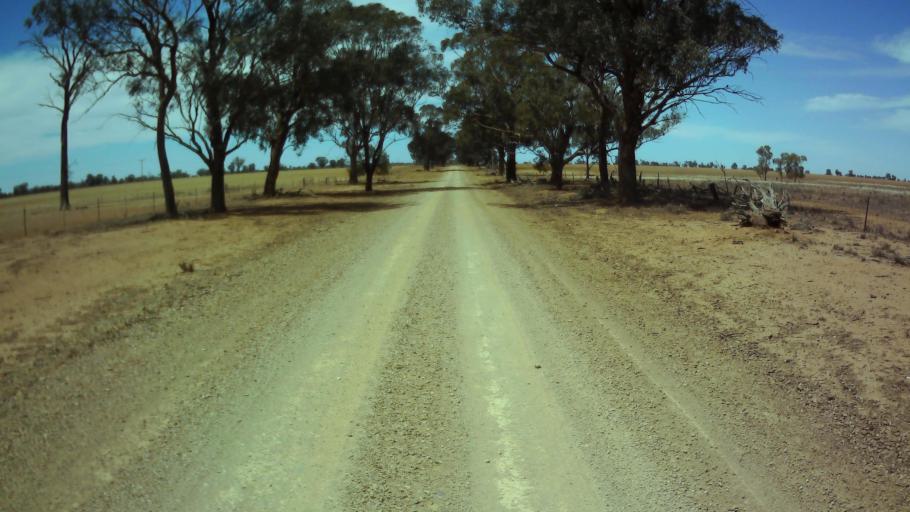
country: AU
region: New South Wales
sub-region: Weddin
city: Grenfell
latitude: -33.8673
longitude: 147.8070
